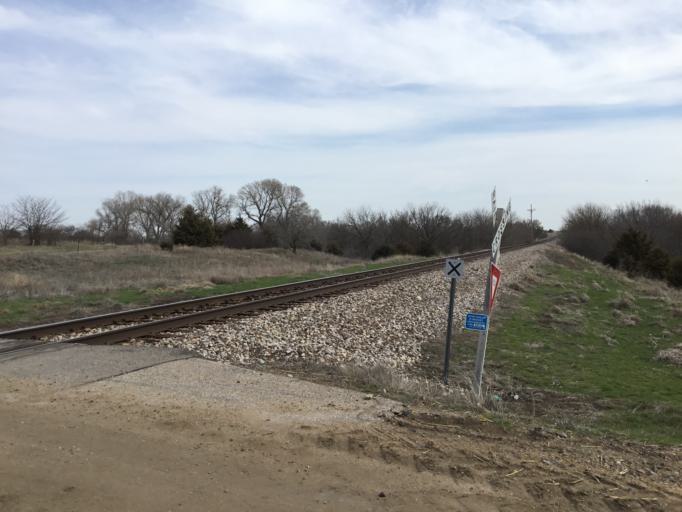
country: US
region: Kansas
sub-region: Ellsworth County
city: Ellsworth
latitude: 38.7240
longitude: -98.1327
